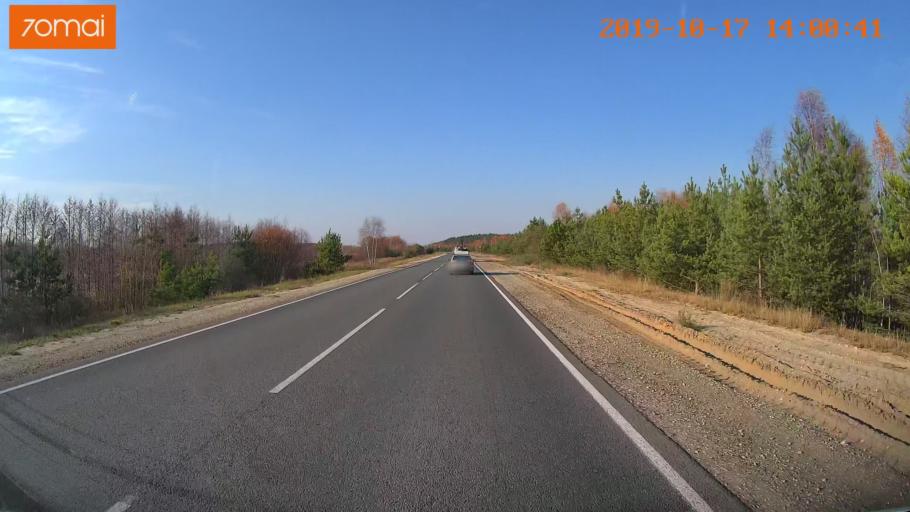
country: RU
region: Rjazan
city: Spas-Klepiki
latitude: 55.1476
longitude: 40.1763
